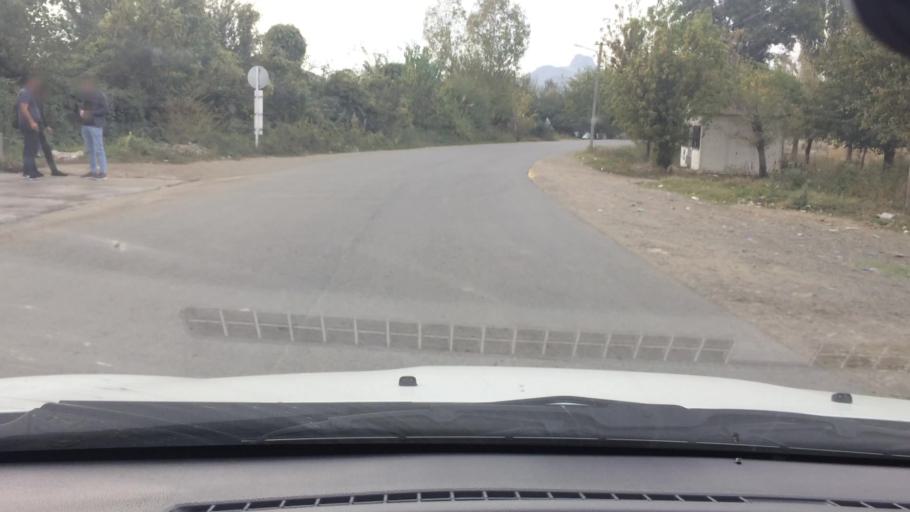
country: GE
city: Naghvarevi
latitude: 41.3541
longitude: 44.8605
